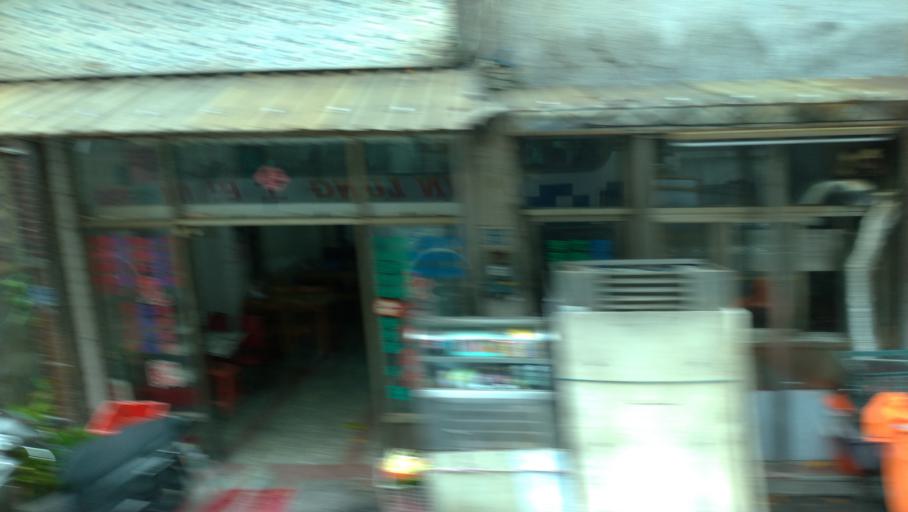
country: TW
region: Taiwan
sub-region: Keelung
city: Keelung
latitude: 25.1436
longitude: 121.7613
